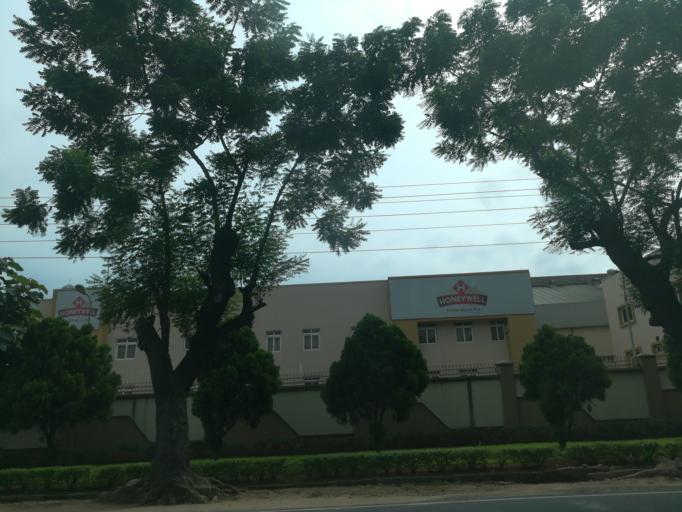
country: NG
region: Lagos
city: Ikeja
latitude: 6.6123
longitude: 3.3663
